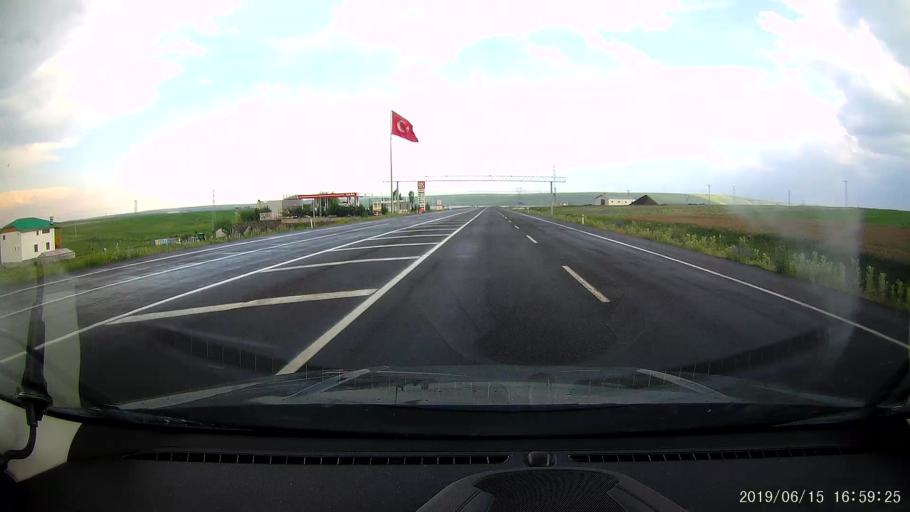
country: TR
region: Kars
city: Susuz
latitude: 40.7522
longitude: 43.1505
